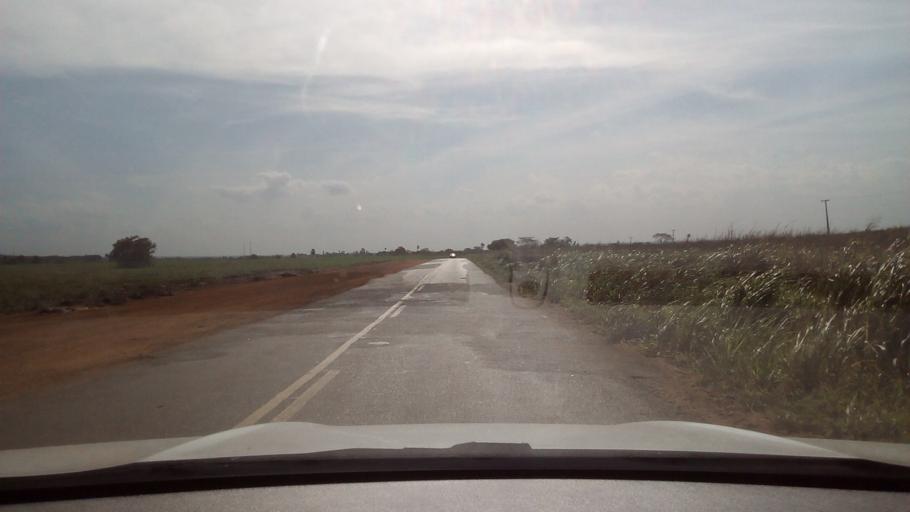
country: BR
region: Rio Grande do Norte
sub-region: Goianinha
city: Goianinha
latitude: -6.2523
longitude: -35.1874
